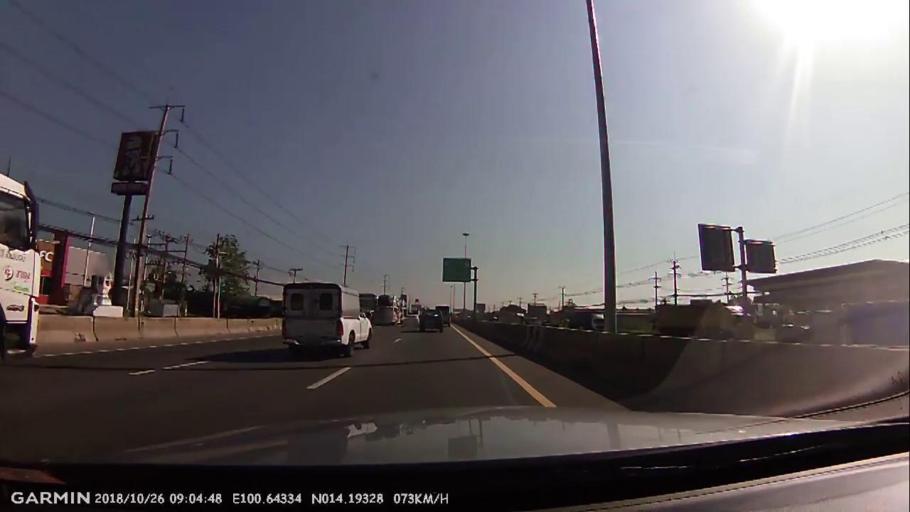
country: TH
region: Phra Nakhon Si Ayutthaya
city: Bang Pa-in
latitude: 14.1941
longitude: 100.6441
